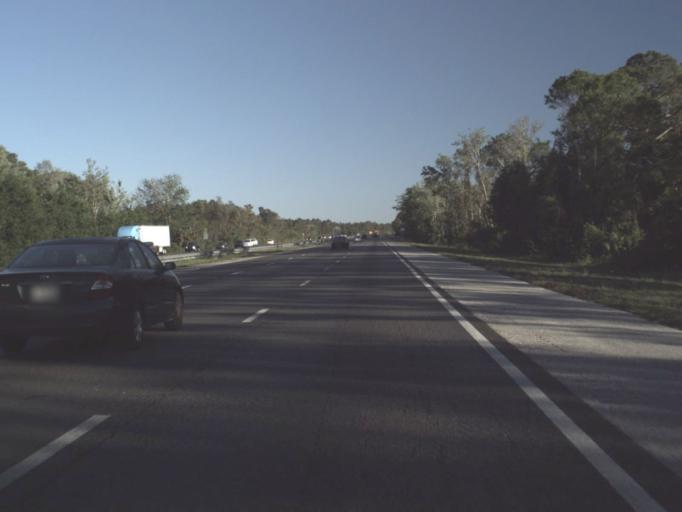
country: US
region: Florida
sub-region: Flagler County
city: Palm Coast
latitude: 29.5424
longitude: -81.2114
